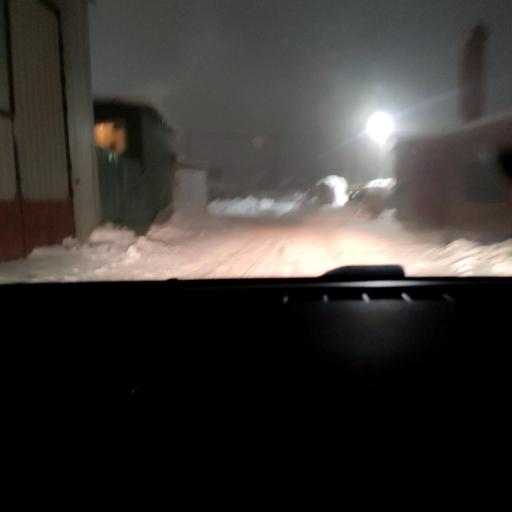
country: RU
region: Samara
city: Samara
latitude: 53.1729
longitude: 50.1687
